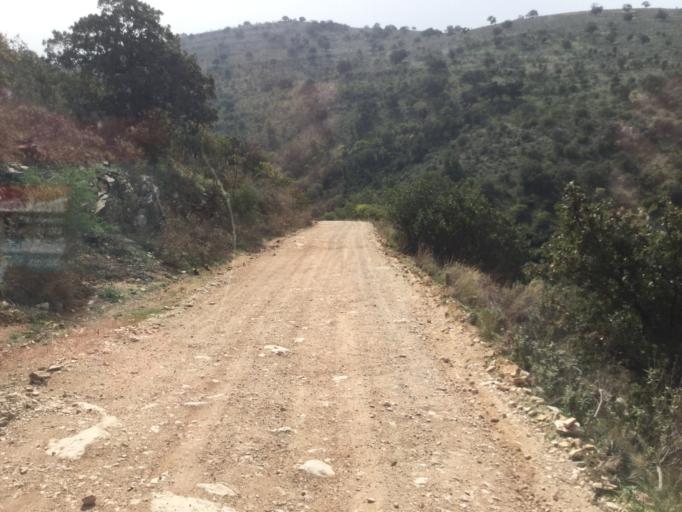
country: GR
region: West Greece
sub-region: Nomos Achaias
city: Lapas
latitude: 38.1753
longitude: 21.3748
